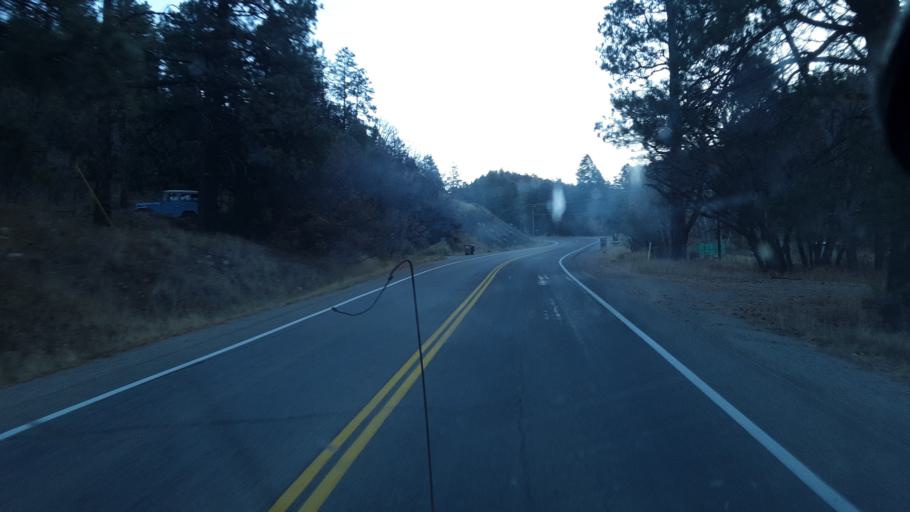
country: US
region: Colorado
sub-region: La Plata County
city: Durango
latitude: 37.3069
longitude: -107.8207
